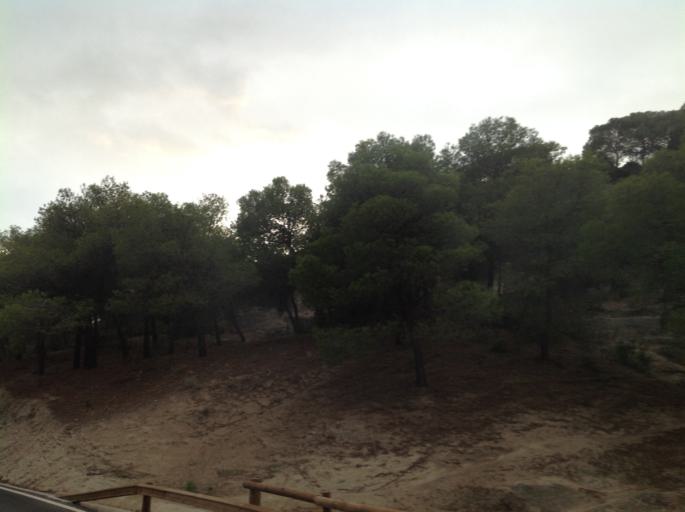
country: ES
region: Andalusia
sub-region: Provincia de Malaga
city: Ardales
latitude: 36.9133
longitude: -4.7964
